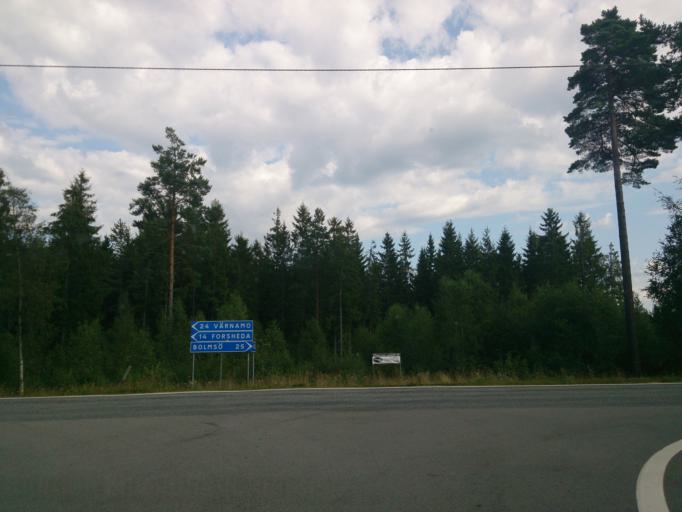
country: SE
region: Joenkoeping
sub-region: Varnamo Kommun
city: Forsheda
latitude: 57.0621
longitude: 13.8502
